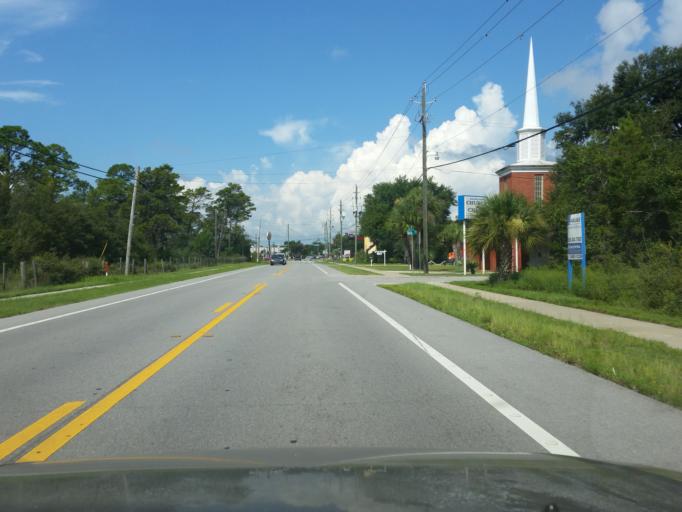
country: US
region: Florida
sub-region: Escambia County
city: Myrtle Grove
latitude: 30.3192
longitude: -87.4213
